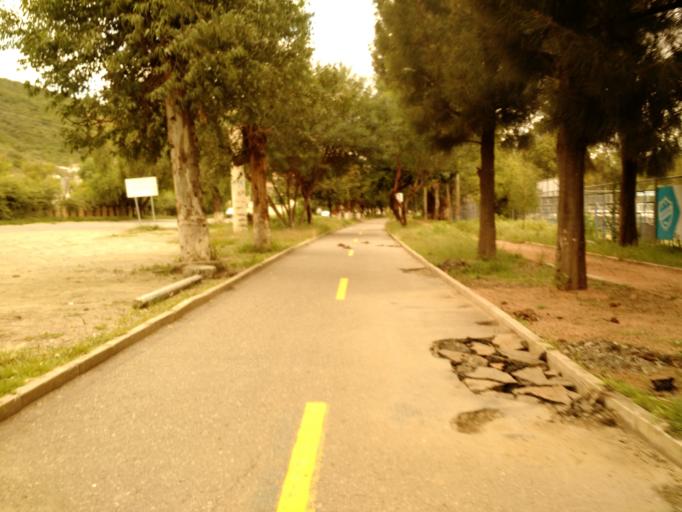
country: BO
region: Cochabamba
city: Cochabamba
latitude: -17.4070
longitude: -66.1280
